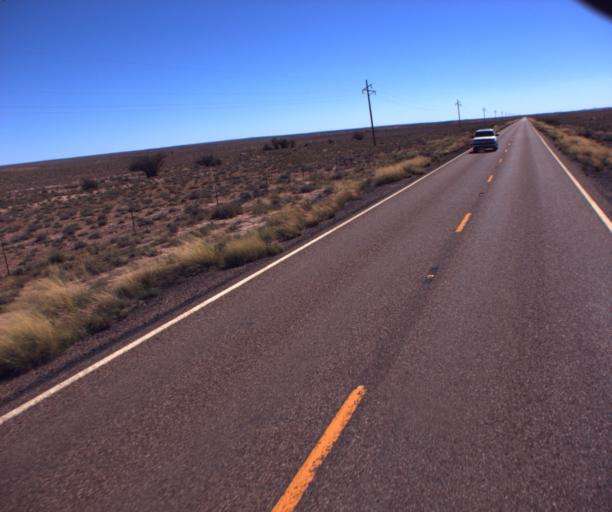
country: US
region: Arizona
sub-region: Navajo County
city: Holbrook
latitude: 35.1029
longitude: -110.0954
